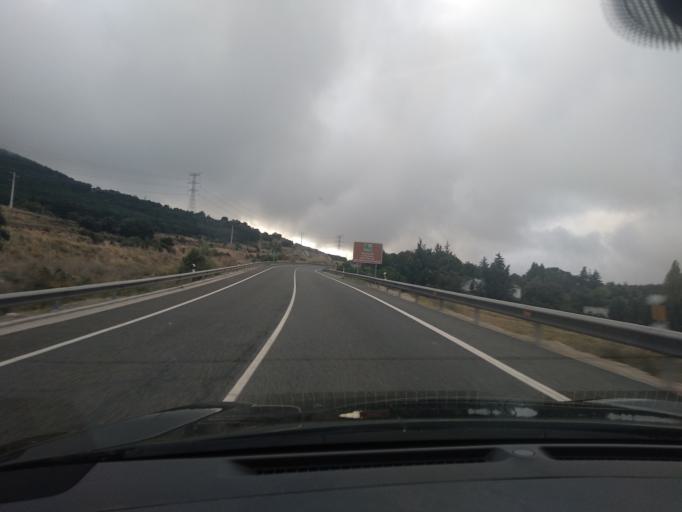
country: ES
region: Castille and Leon
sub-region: Provincia de Segovia
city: Otero de Herreros
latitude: 40.7833
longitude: -4.2121
